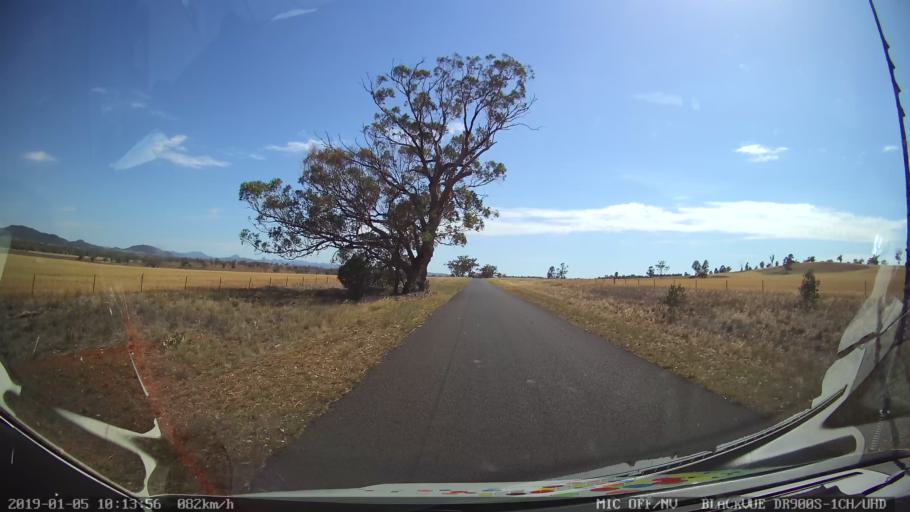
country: AU
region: New South Wales
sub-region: Gilgandra
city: Gilgandra
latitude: -31.5975
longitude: 148.9297
